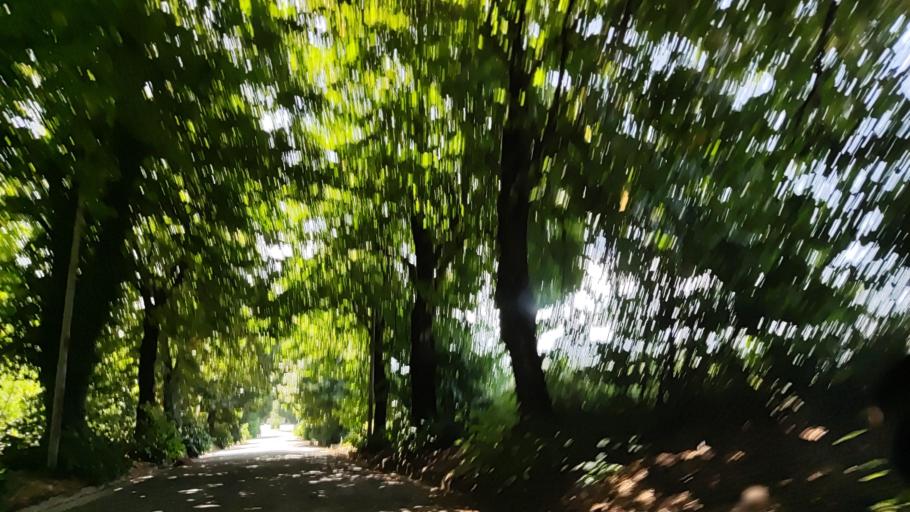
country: IT
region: Calabria
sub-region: Provincia di Reggio Calabria
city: Seminara
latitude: 38.3351
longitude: 15.8464
